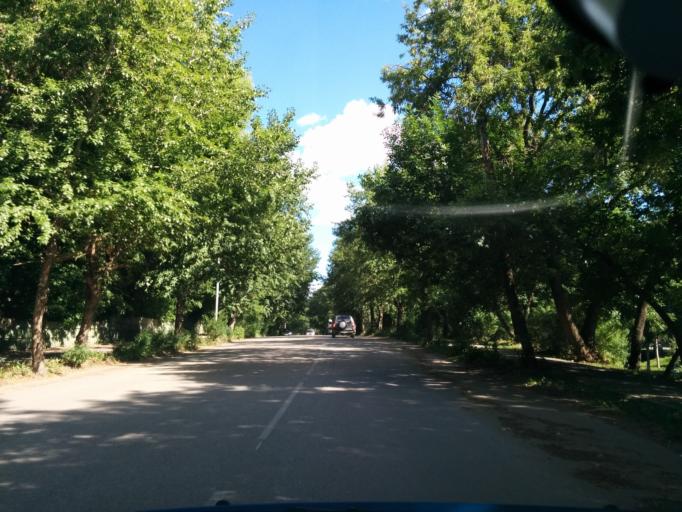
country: RU
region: Perm
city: Perm
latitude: 58.0081
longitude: 56.1953
